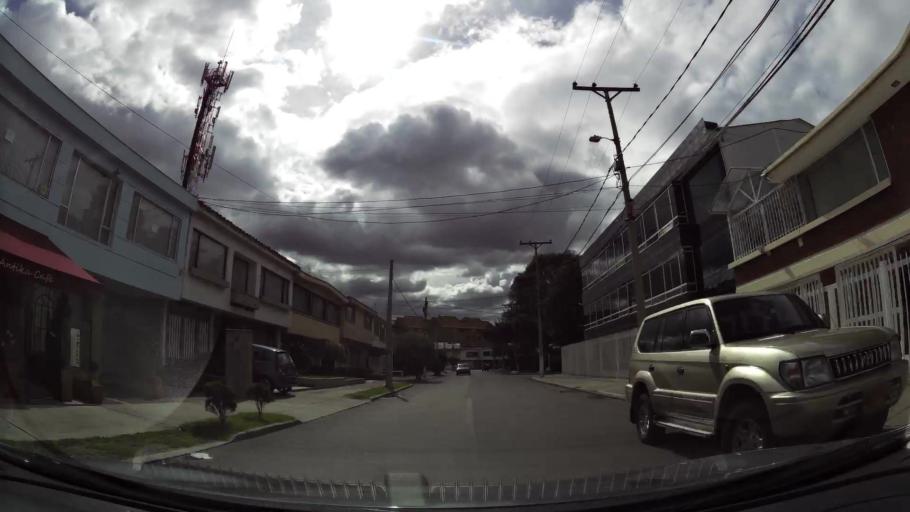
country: CO
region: Bogota D.C.
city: Barrio San Luis
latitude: 4.6883
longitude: -74.0593
